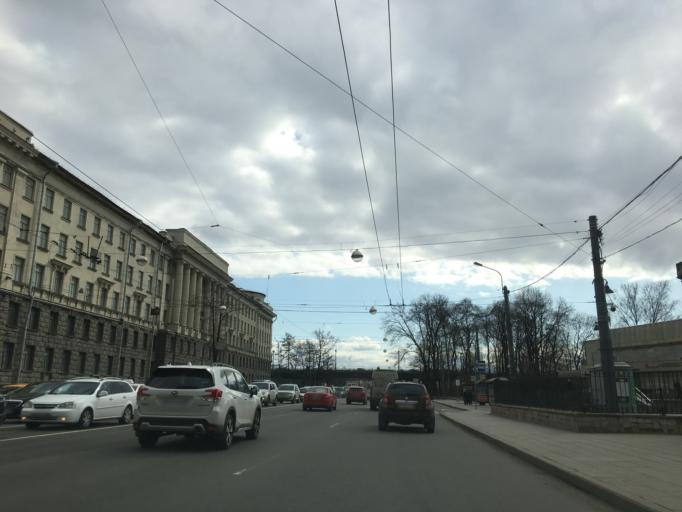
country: RU
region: Leningrad
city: Chernaya Rechka
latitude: 59.9859
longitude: 30.3018
